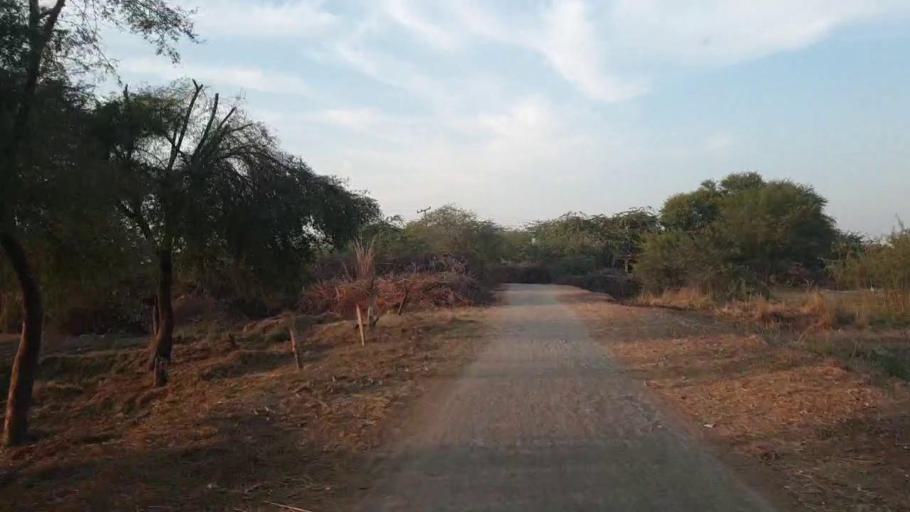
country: PK
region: Sindh
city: Shahpur Chakar
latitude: 26.1832
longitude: 68.6180
